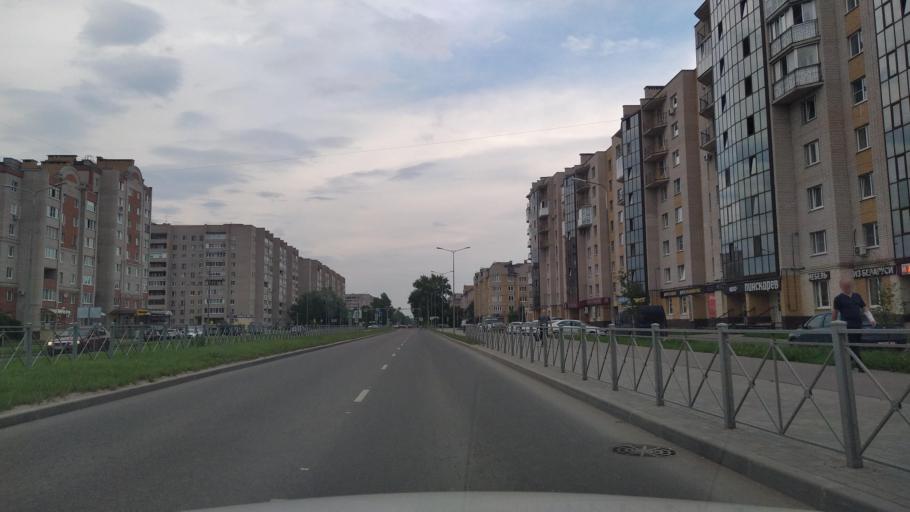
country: RU
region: Novgorod
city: Pankovka
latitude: 58.5077
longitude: 31.2317
